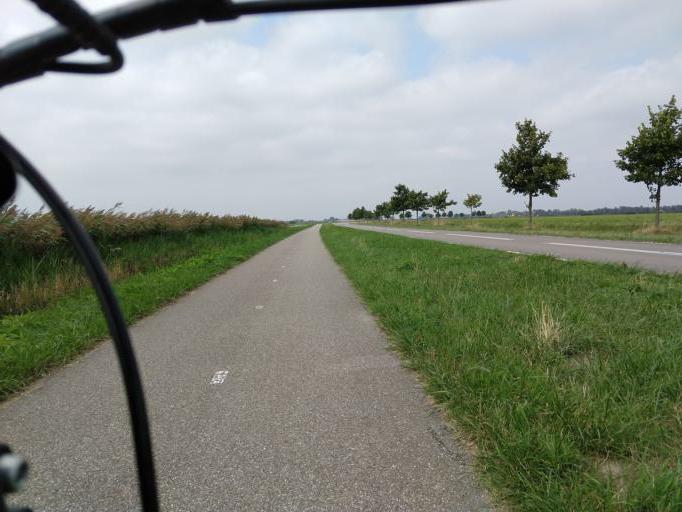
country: NL
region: Zeeland
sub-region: Schouwen-Duiveland
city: Bruinisse
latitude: 51.6552
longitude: 4.0821
